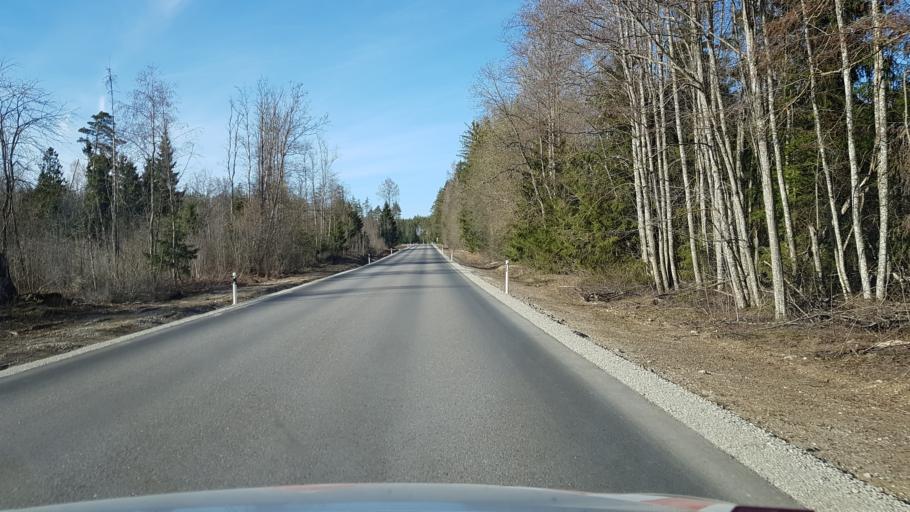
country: EE
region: Laeaene-Virumaa
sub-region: Vinni vald
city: Vinni
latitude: 59.1199
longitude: 26.6179
